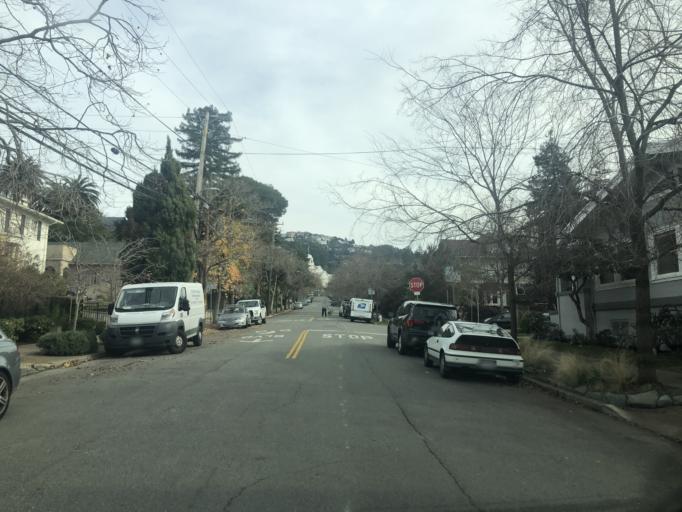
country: US
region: California
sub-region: Alameda County
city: Berkeley
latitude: 37.8588
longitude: -122.2490
